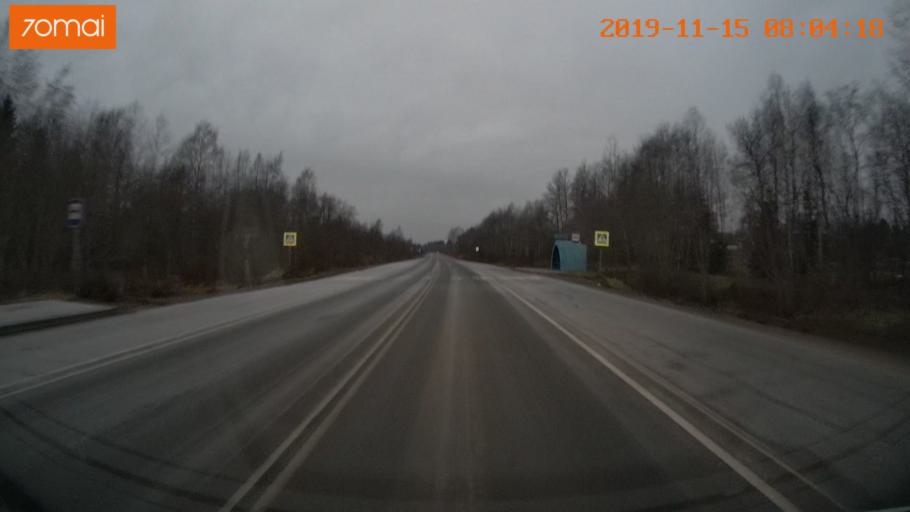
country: RU
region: Vologda
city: Cherepovets
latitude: 59.0064
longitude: 38.0790
